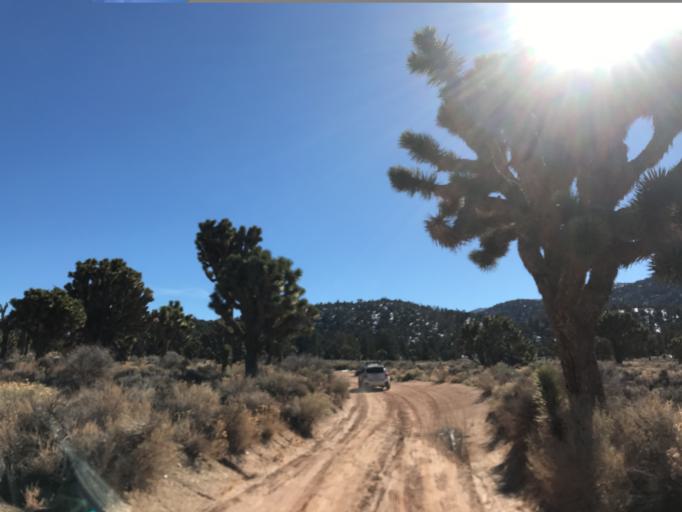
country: US
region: California
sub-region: San Bernardino County
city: Big Bear City
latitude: 34.2483
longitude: -116.7045
